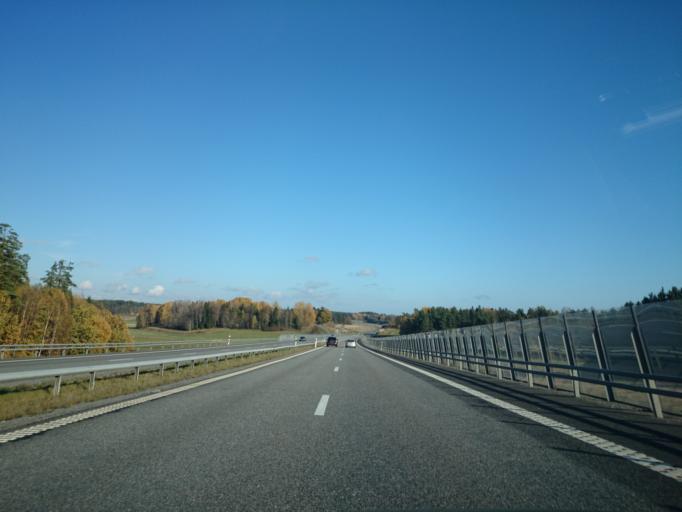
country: SE
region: Stockholm
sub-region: Haninge Kommun
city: Jordbro
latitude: 59.0613
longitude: 18.0354
